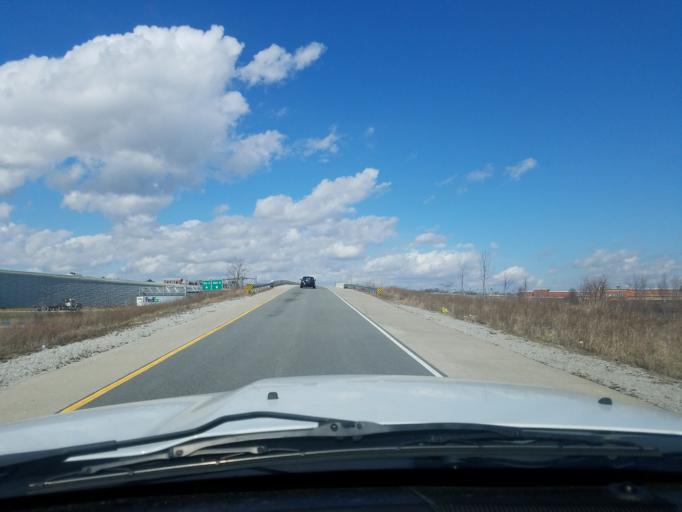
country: US
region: Indiana
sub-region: Hamilton County
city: Carmel
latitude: 39.9955
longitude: -86.1247
